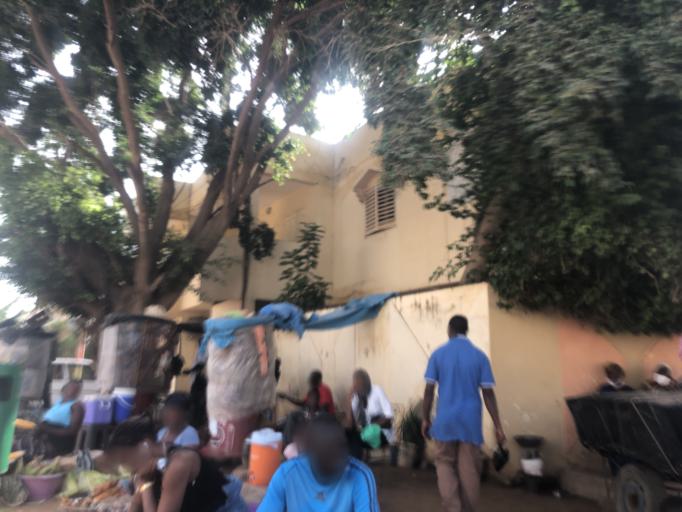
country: SN
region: Dakar
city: Mermoz Boabab
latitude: 14.7326
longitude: -17.4932
